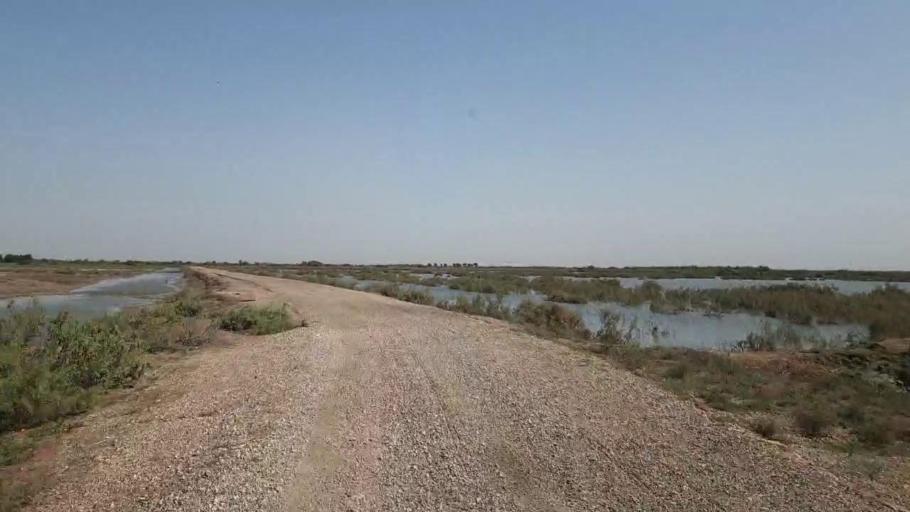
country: PK
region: Sindh
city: Tando Bago
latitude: 24.7299
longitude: 69.0346
